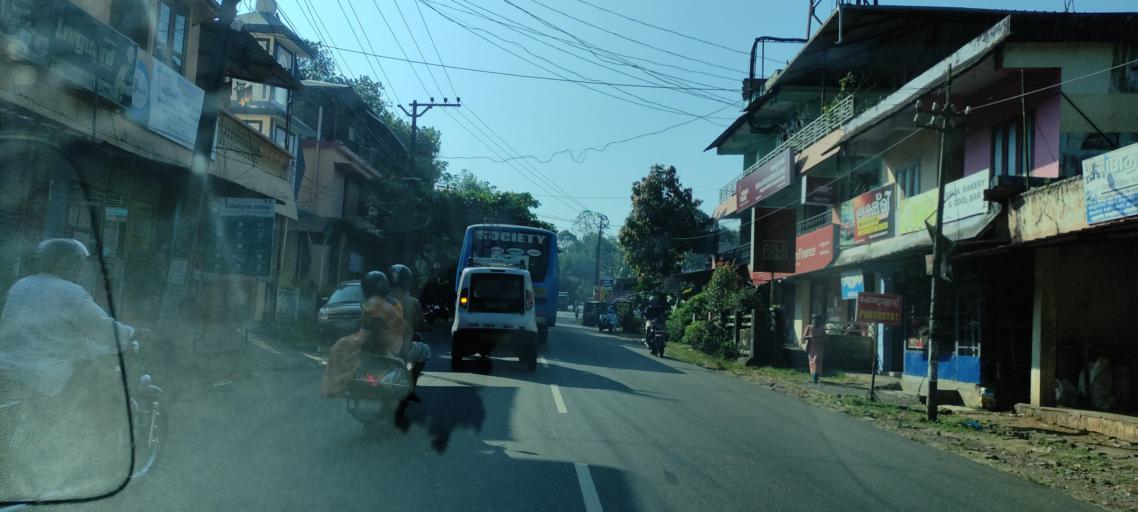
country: IN
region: Kerala
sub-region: Pattanamtitta
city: Adur
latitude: 9.1216
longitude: 76.7002
